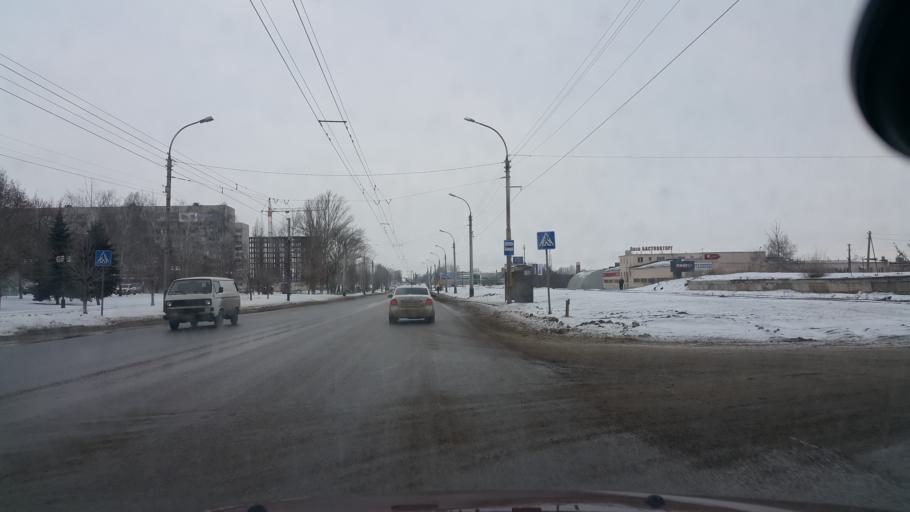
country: RU
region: Tambov
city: Tambov
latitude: 52.7372
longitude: 41.3833
